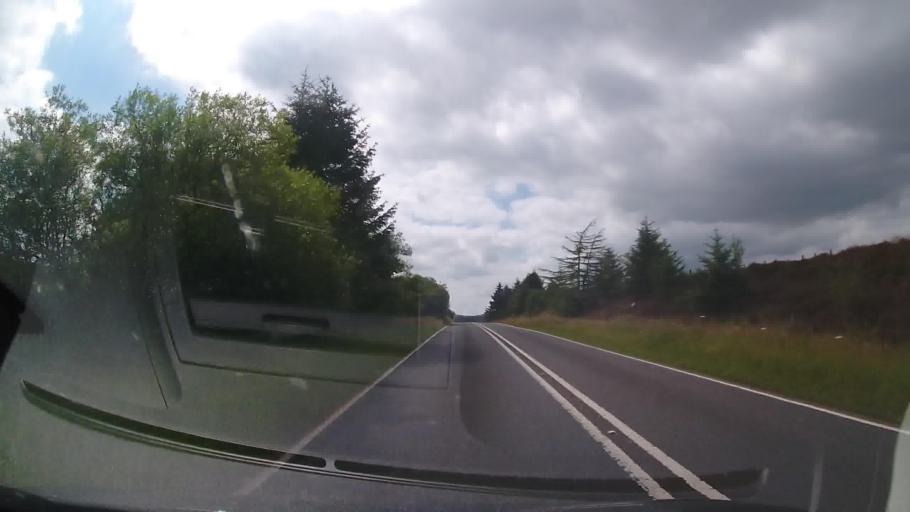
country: GB
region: Wales
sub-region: Gwynedd
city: Trawsfynydd
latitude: 52.9287
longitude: -3.7932
